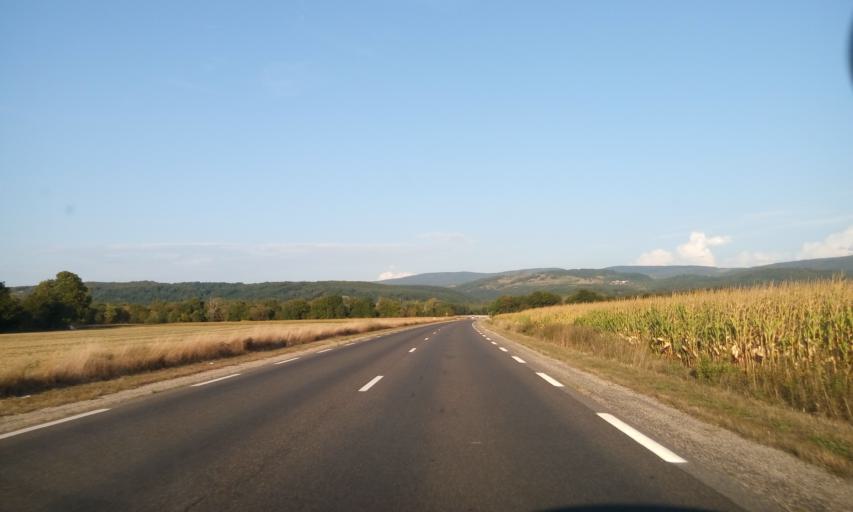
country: FR
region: Rhone-Alpes
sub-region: Departement de l'Ain
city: Saint-Jean-le-Vieux
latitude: 46.0427
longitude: 5.3650
